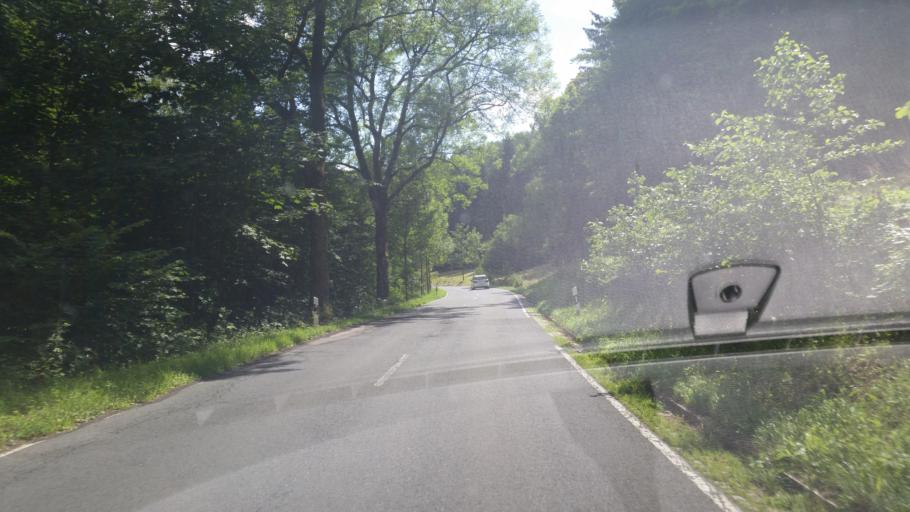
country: DE
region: Saxony
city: Glashutte
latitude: 50.8395
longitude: 13.7313
